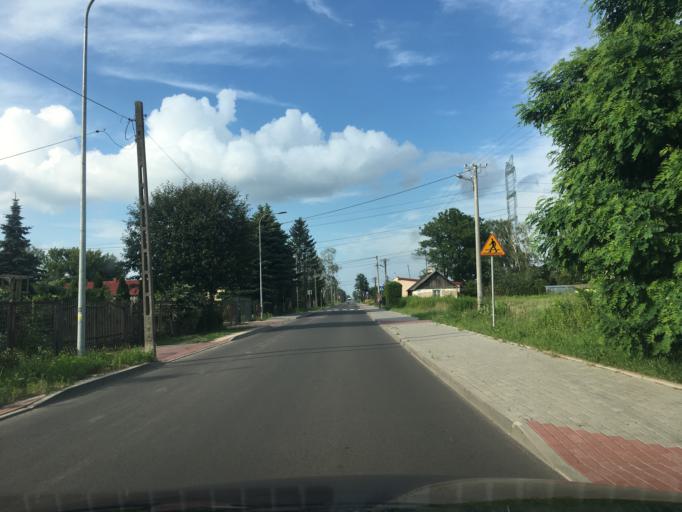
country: PL
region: Masovian Voivodeship
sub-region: Powiat wolominski
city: Radzymin
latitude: 52.4042
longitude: 21.2084
